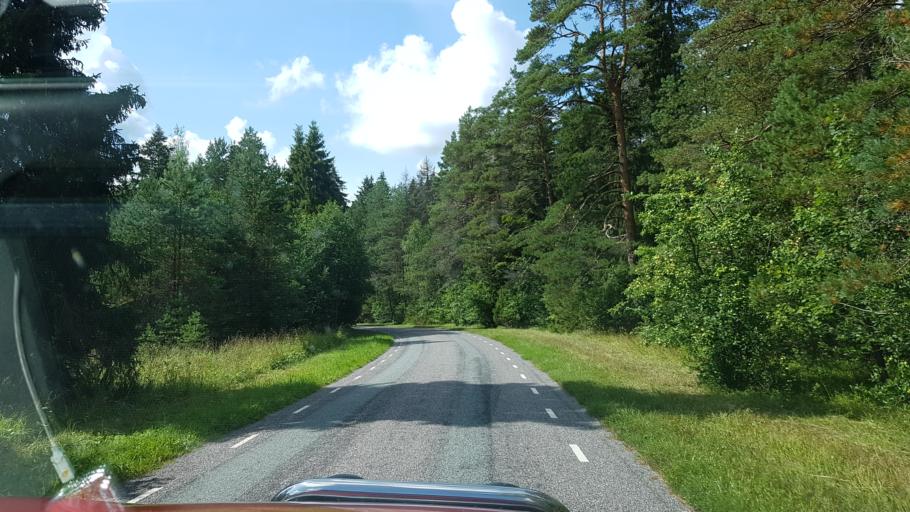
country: EE
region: Raplamaa
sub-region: Rapla vald
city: Rapla
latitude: 58.9638
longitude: 24.6095
